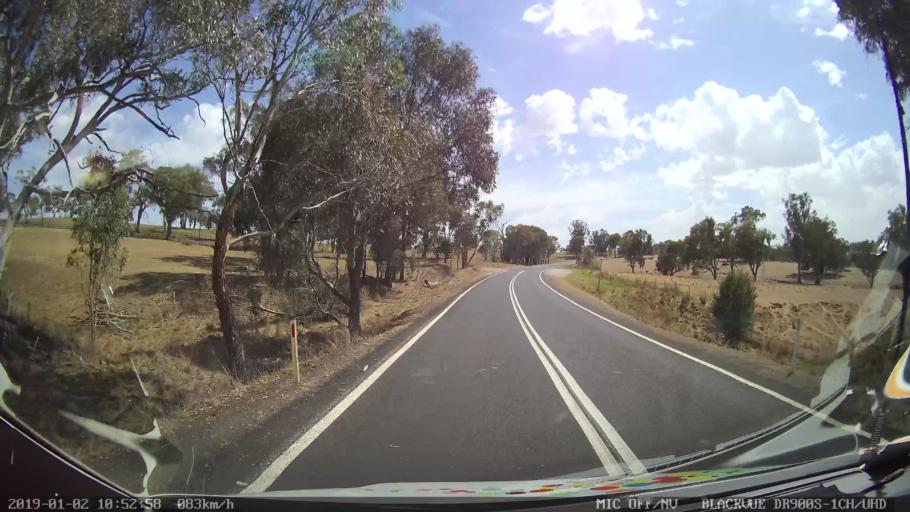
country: AU
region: New South Wales
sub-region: Cootamundra
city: Cootamundra
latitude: -34.6825
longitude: 148.2715
